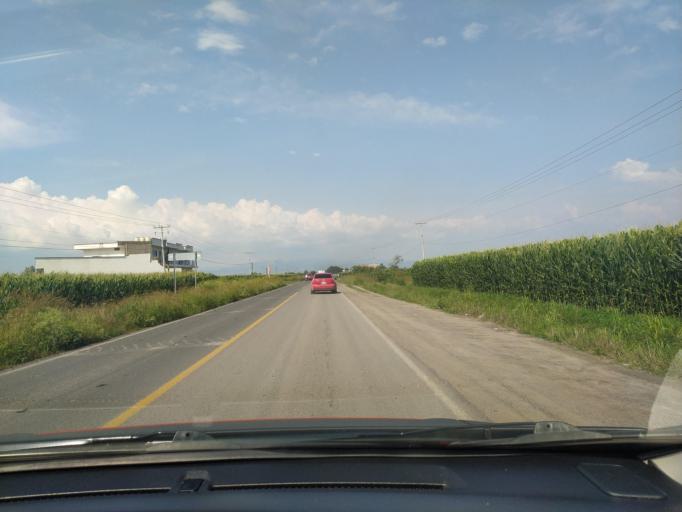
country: MX
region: Guanajuato
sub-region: Leon
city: Malagana (San Antonio del Monte)
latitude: 21.0501
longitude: -101.7522
